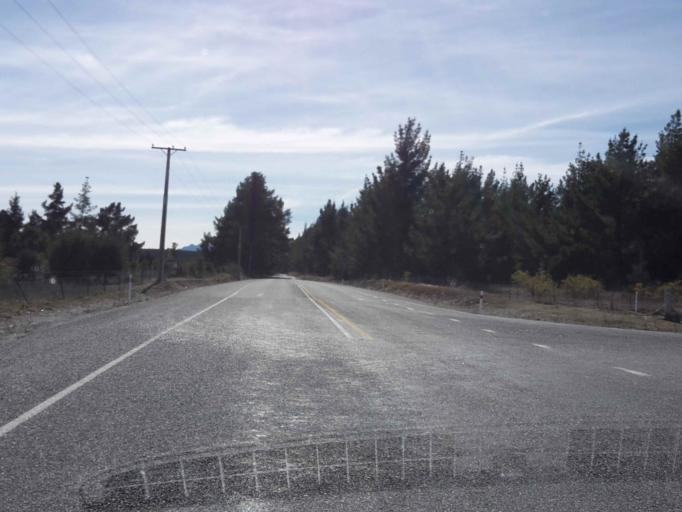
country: NZ
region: Otago
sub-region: Queenstown-Lakes District
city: Wanaka
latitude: -44.7287
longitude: 169.2822
